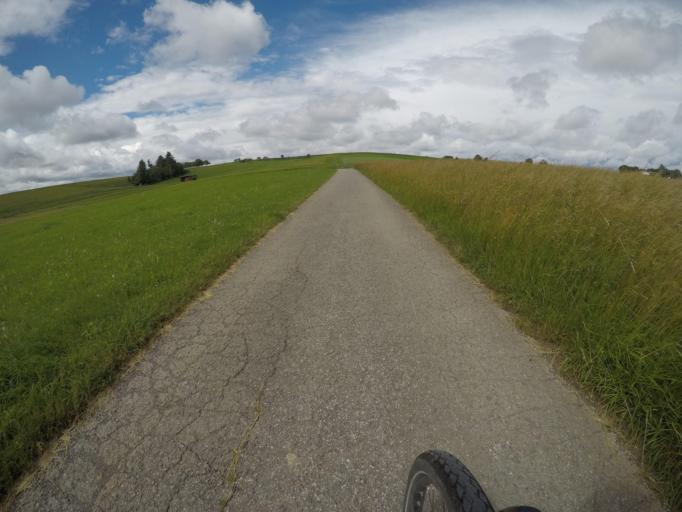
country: DE
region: Baden-Wuerttemberg
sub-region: Regierungsbezirk Stuttgart
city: Deckenpfronn
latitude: 48.6392
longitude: 8.8464
